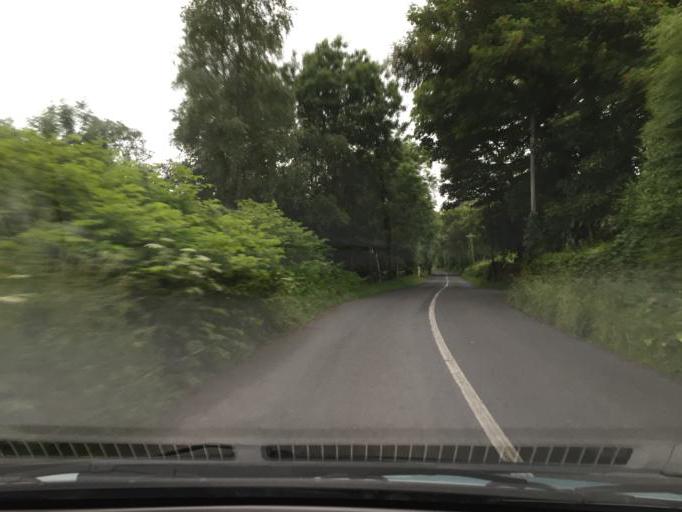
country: IE
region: Connaught
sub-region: Sligo
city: Sligo
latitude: 54.2648
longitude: -8.5116
